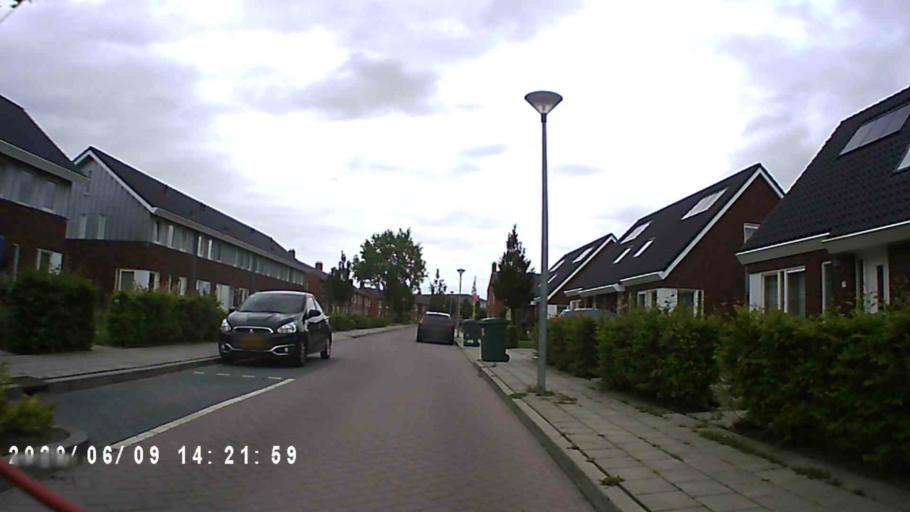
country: NL
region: Groningen
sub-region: Gemeente Bedum
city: Bedum
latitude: 53.2985
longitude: 6.5920
